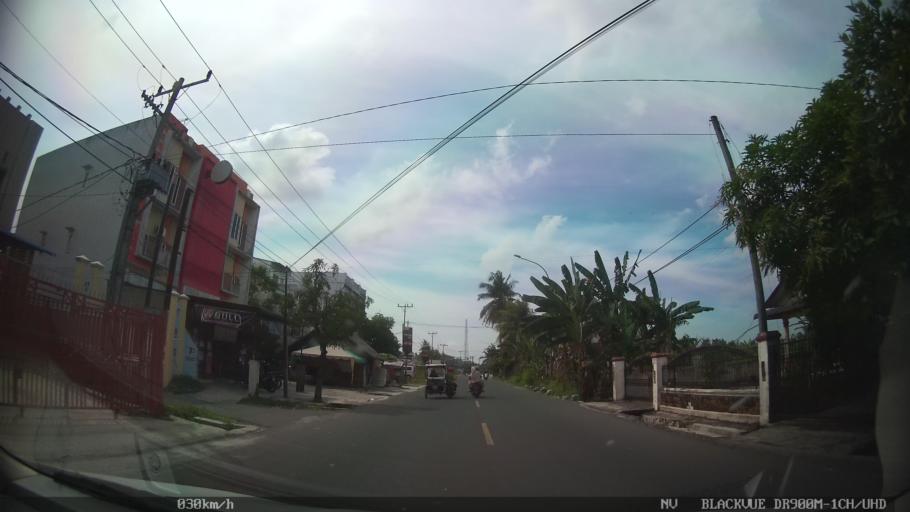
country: ID
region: North Sumatra
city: Percut
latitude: 3.5792
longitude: 98.8643
